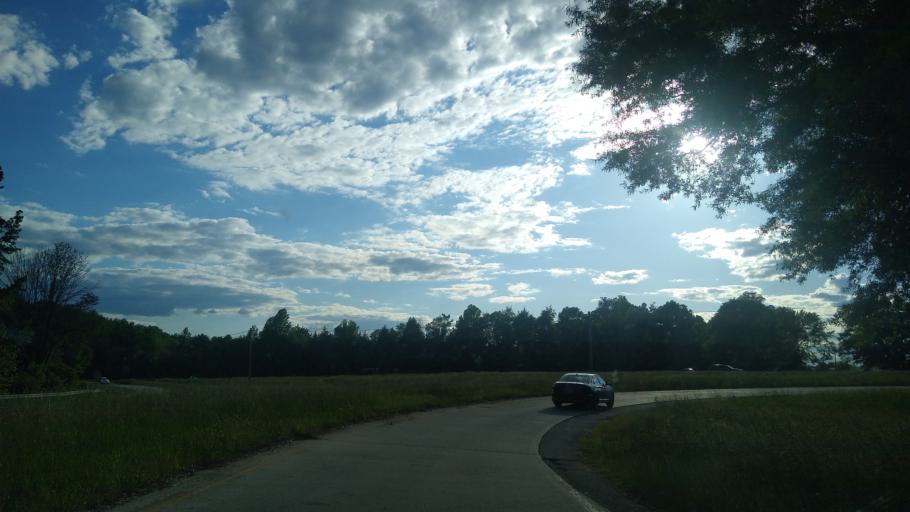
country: US
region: North Carolina
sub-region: Guilford County
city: McLeansville
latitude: 36.1746
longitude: -79.7112
